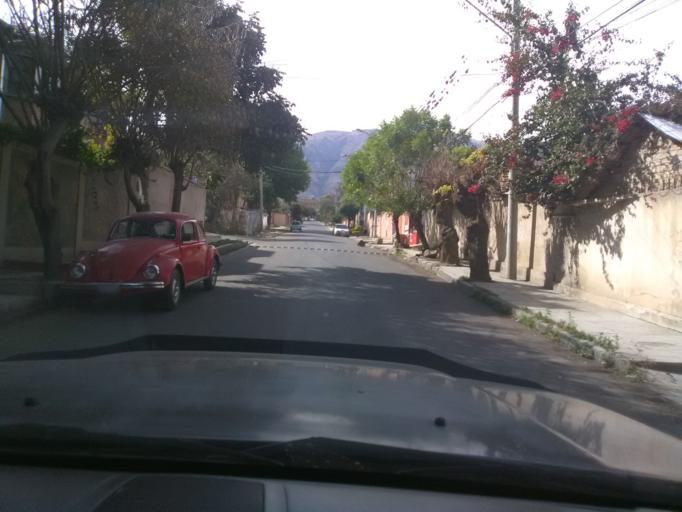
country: BO
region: Cochabamba
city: Cochabamba
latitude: -17.3635
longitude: -66.1704
